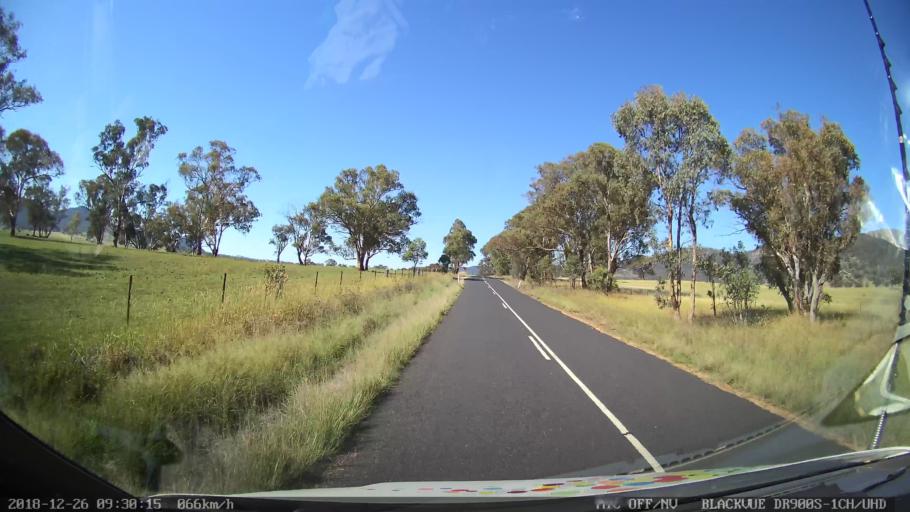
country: AU
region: New South Wales
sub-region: Mid-Western Regional
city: Kandos
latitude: -32.8611
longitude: 150.0299
